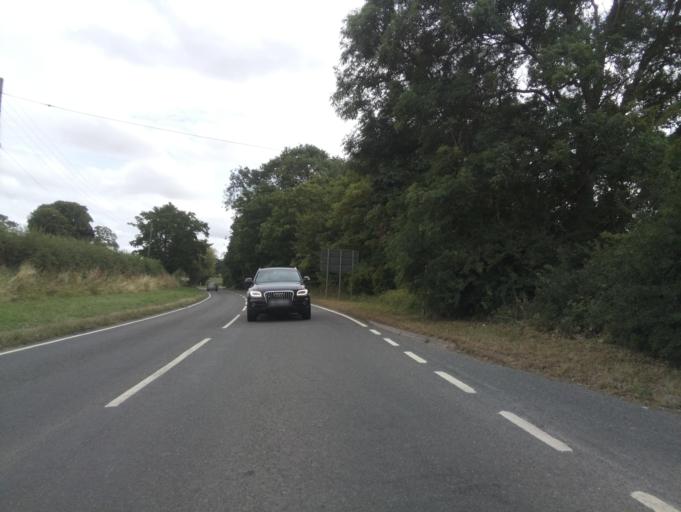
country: GB
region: England
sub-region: Derbyshire
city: Melbourne
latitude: 52.8100
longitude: -1.3789
